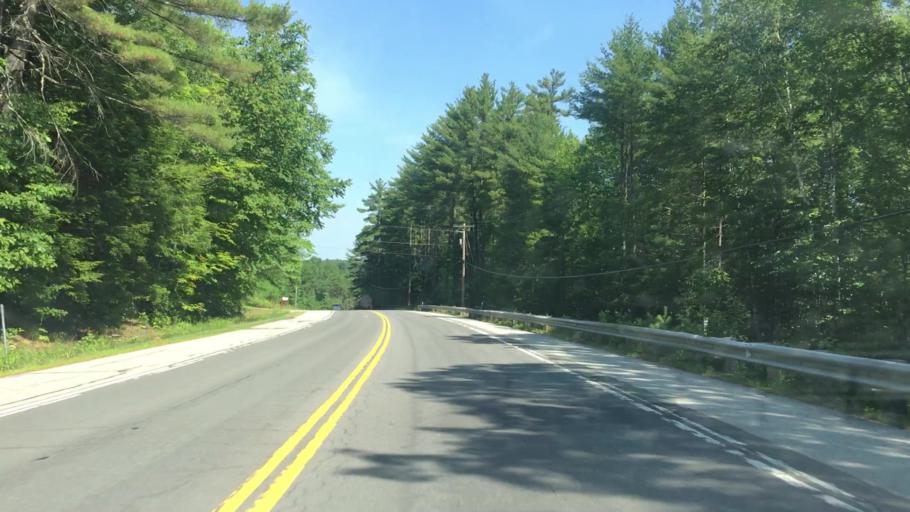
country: US
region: New Hampshire
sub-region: Merrimack County
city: Sutton
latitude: 43.2440
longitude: -71.9224
